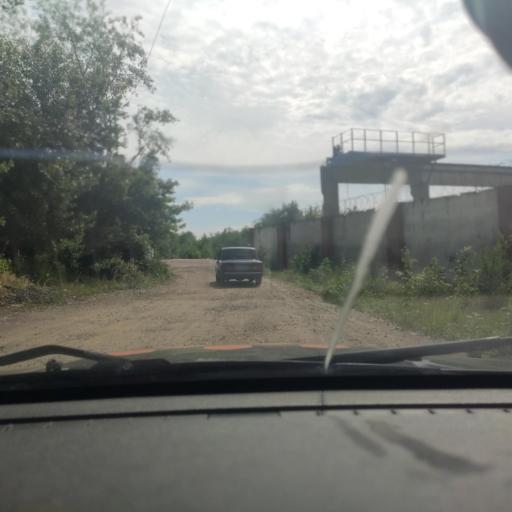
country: RU
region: Samara
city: Zhigulevsk
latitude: 53.4658
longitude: 49.5706
